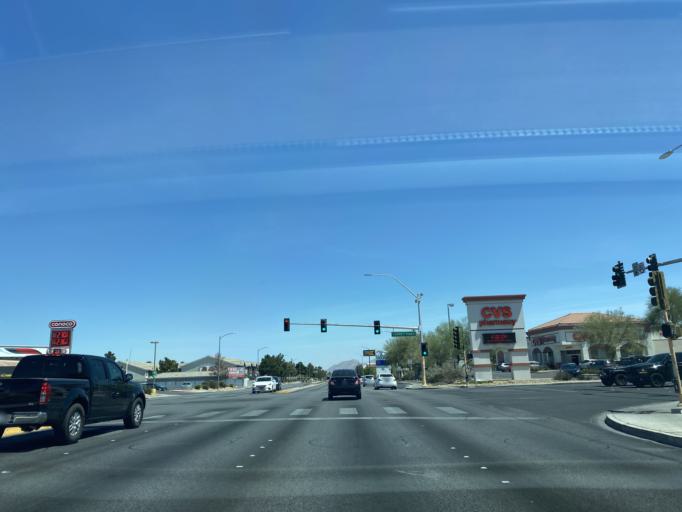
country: US
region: Nevada
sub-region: Clark County
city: Spring Valley
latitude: 36.1958
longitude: -115.2336
